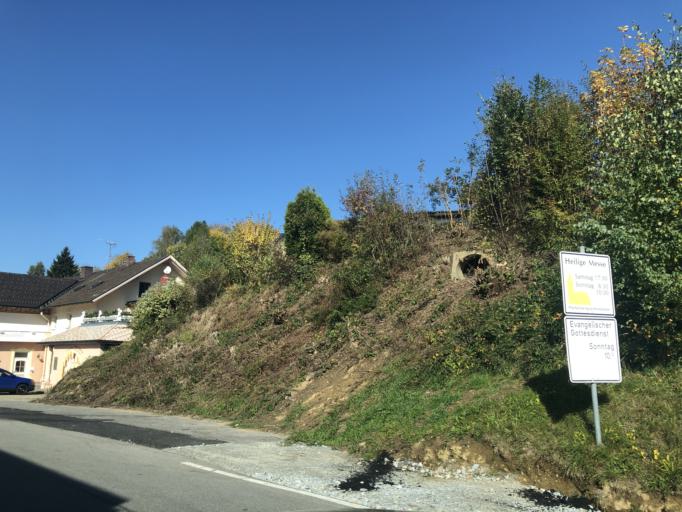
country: DE
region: Bavaria
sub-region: Lower Bavaria
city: Bodenmais
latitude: 49.0634
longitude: 13.1044
